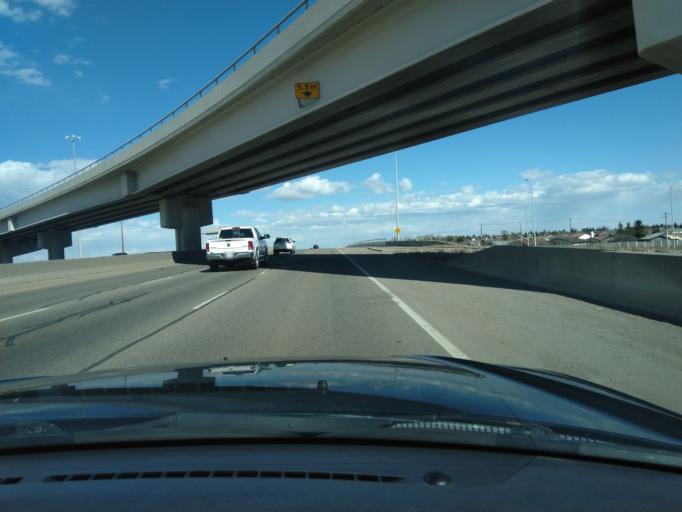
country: CA
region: Alberta
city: Calgary
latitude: 51.0957
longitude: -113.9836
